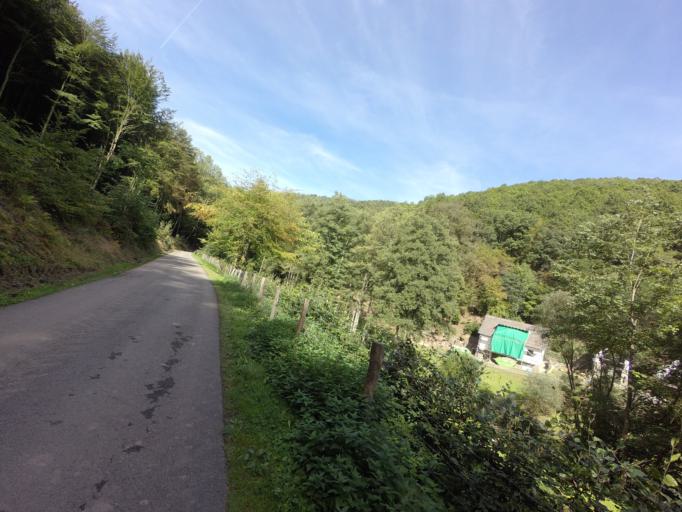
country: DE
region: North Rhine-Westphalia
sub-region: Regierungsbezirk Koln
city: Hurtgenwald
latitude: 50.6383
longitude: 6.3861
